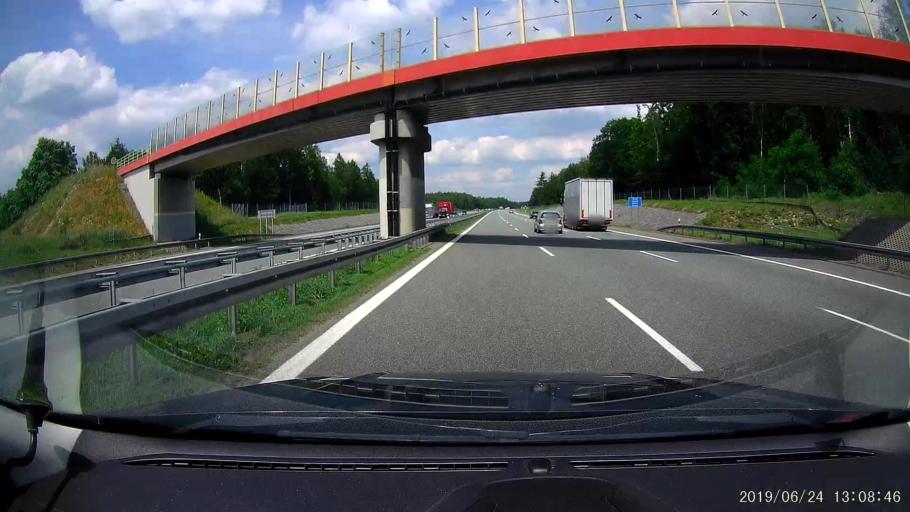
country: PL
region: Silesian Voivodeship
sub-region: Powiat rybnicki
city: Czerwionka-Leszczyny
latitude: 50.1822
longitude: 18.7099
